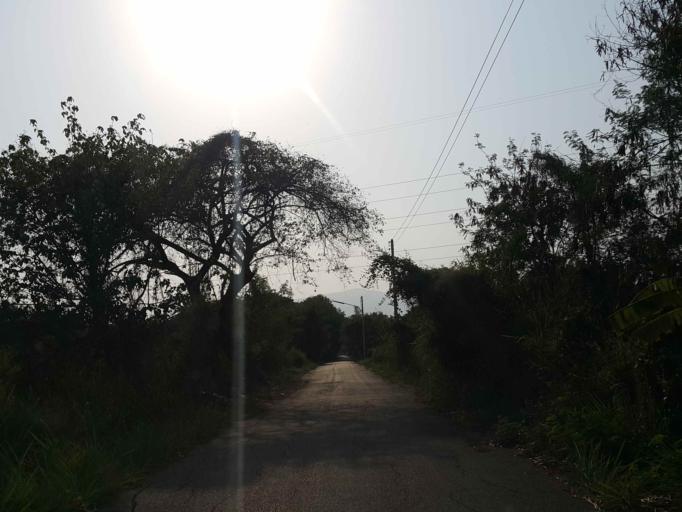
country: TH
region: Chiang Mai
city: Chiang Mai
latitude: 18.7721
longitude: 99.0251
